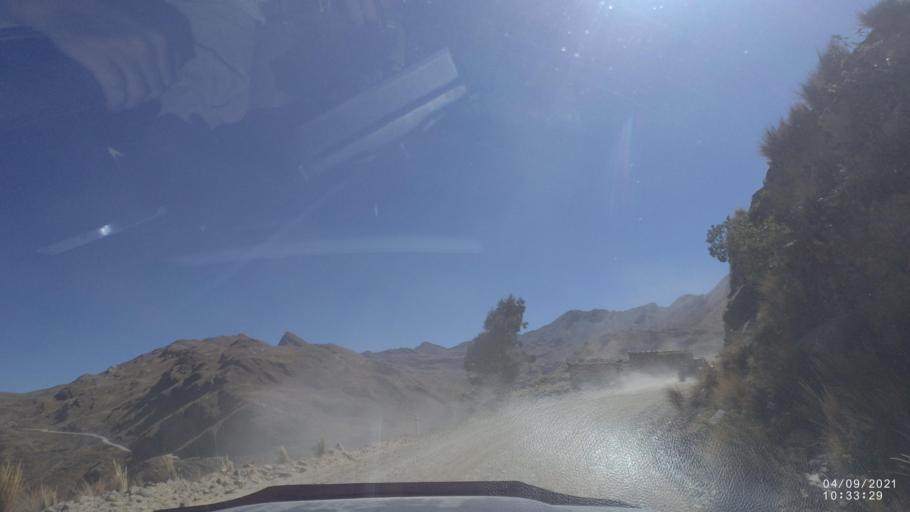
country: BO
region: Cochabamba
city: Sipe Sipe
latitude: -17.2951
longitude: -66.4477
